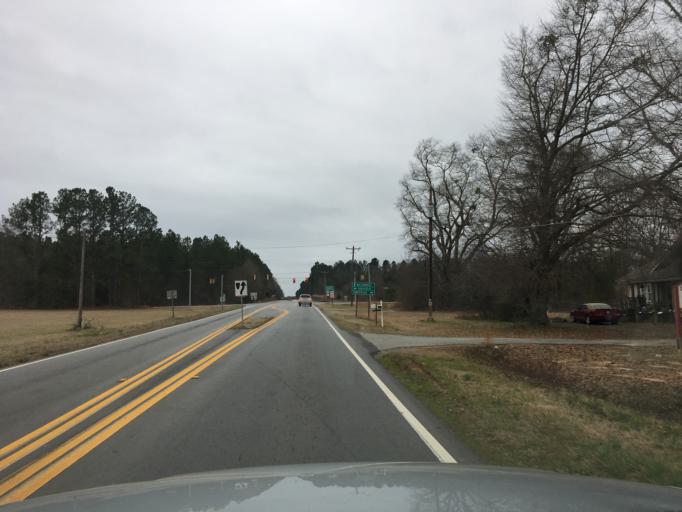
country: US
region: South Carolina
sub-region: Greenwood County
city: Greenwood
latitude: 34.1436
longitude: -82.1477
